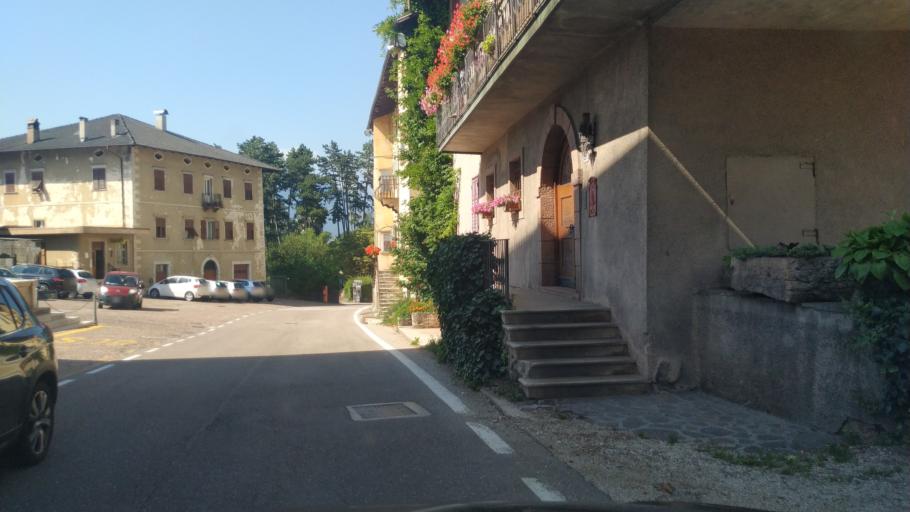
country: IT
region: Trentino-Alto Adige
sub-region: Provincia di Trento
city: Sanzeno
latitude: 46.3658
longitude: 11.0743
